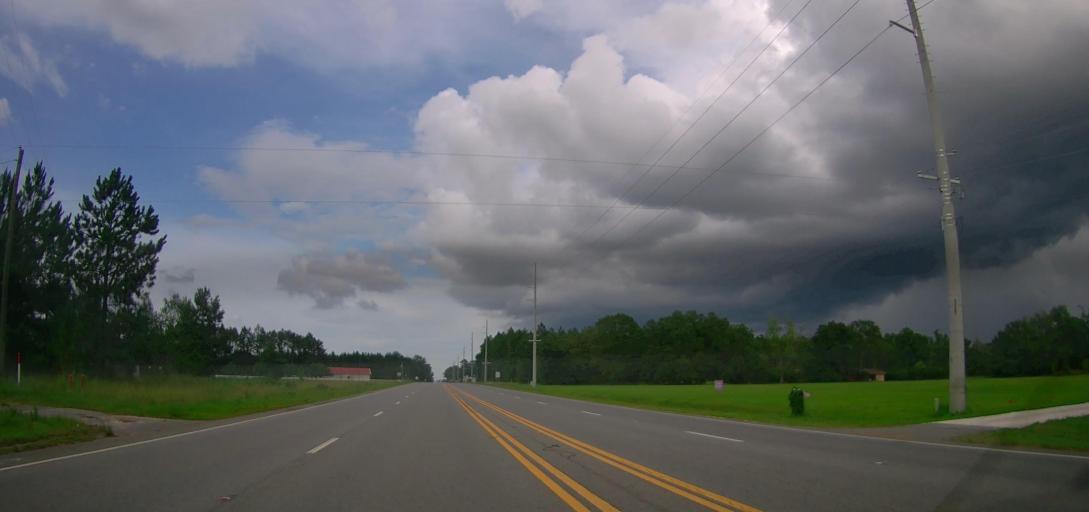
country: US
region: Georgia
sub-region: Pierce County
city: Blackshear
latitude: 31.4047
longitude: -82.1182
